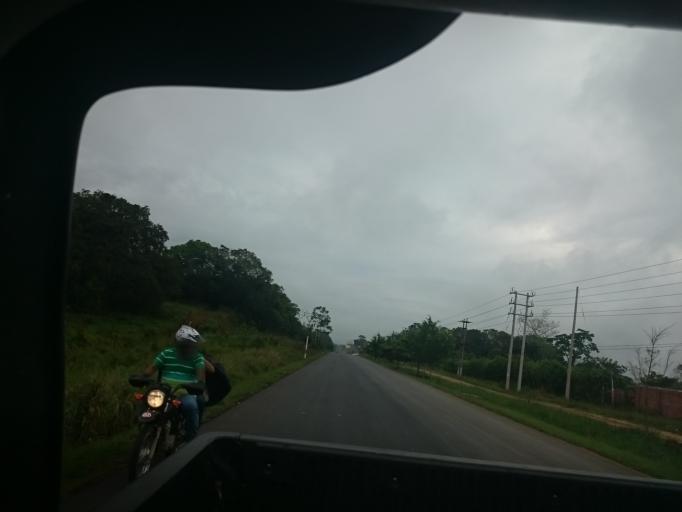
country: PE
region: Ucayali
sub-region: Provincia de Coronel Portillo
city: Campoverde
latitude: -8.4694
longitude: -74.7985
